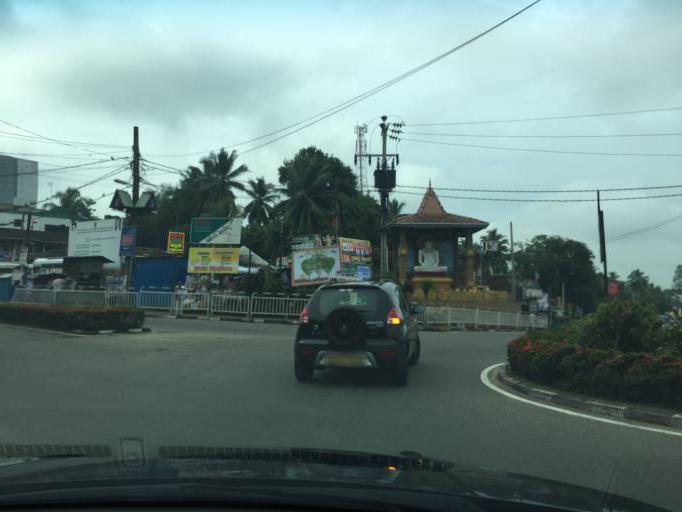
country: LK
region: Western
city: Horana South
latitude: 6.7145
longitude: 79.9891
